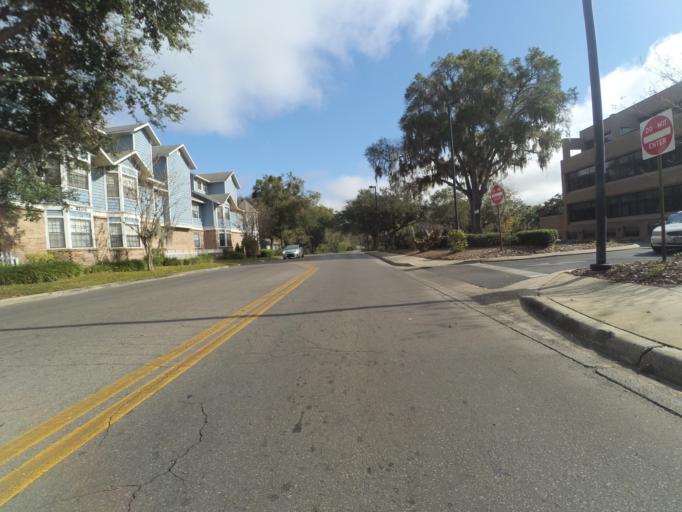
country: US
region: Florida
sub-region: Alachua County
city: Gainesville
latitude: 29.6484
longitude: -82.3221
